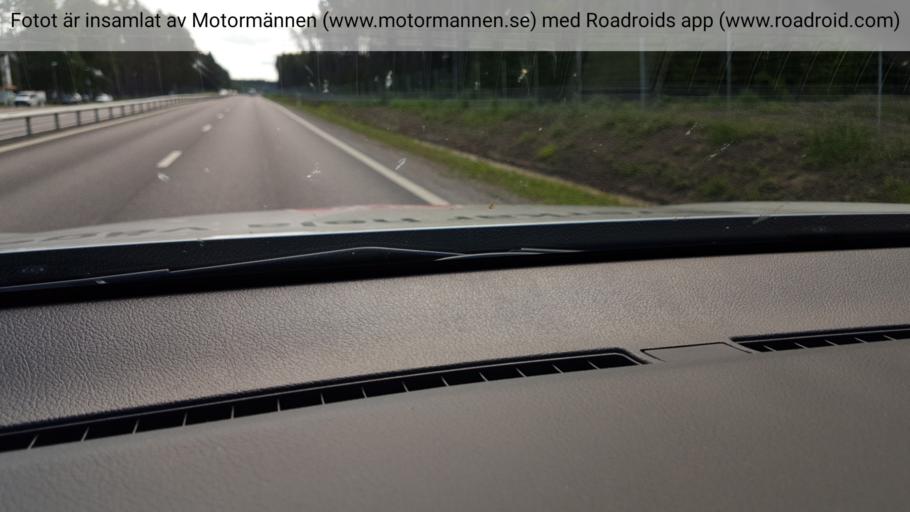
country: SE
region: Vaestra Goetaland
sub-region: Lidkopings Kommun
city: Lidkoping
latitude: 58.4864
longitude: 13.1908
